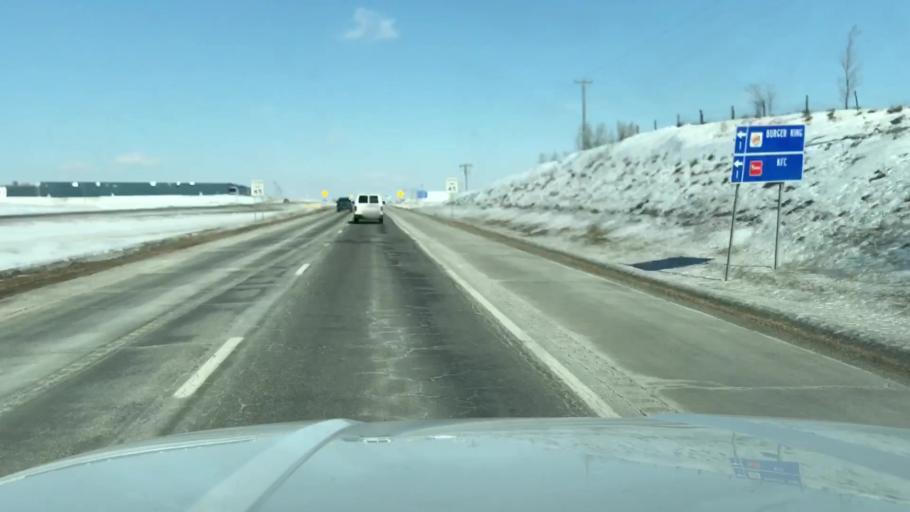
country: US
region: Missouri
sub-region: Nodaway County
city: Maryville
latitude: 40.3057
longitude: -94.8744
